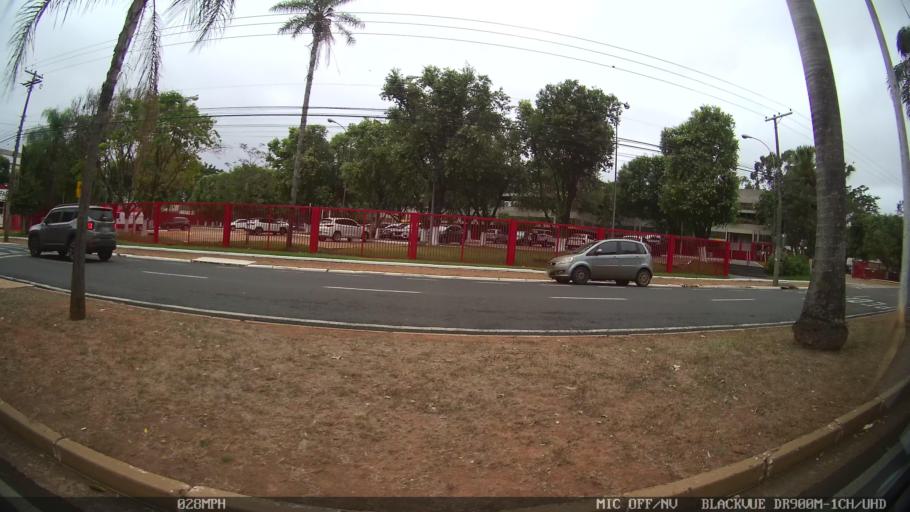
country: BR
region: Sao Paulo
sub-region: Sao Jose Do Rio Preto
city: Sao Jose do Rio Preto
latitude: -20.8384
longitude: -49.4011
